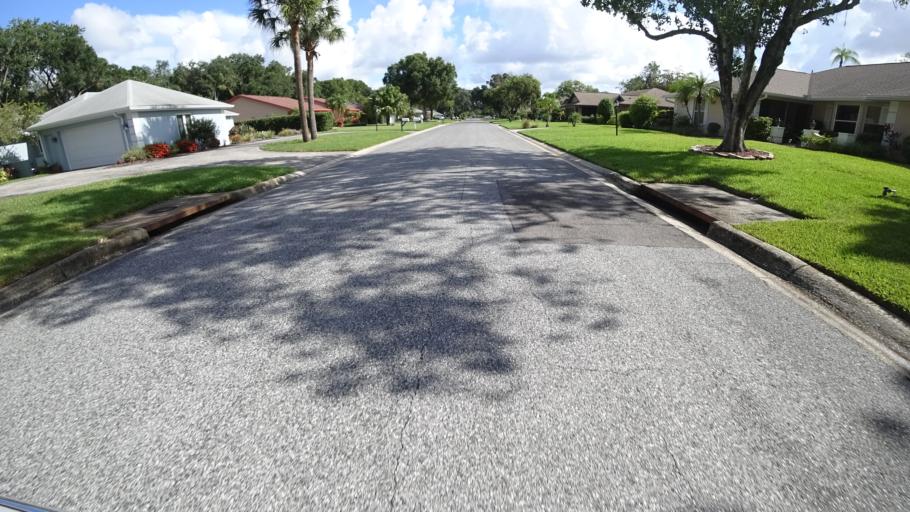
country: US
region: Florida
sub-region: Sarasota County
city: Desoto Lakes
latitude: 27.3937
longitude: -82.4886
